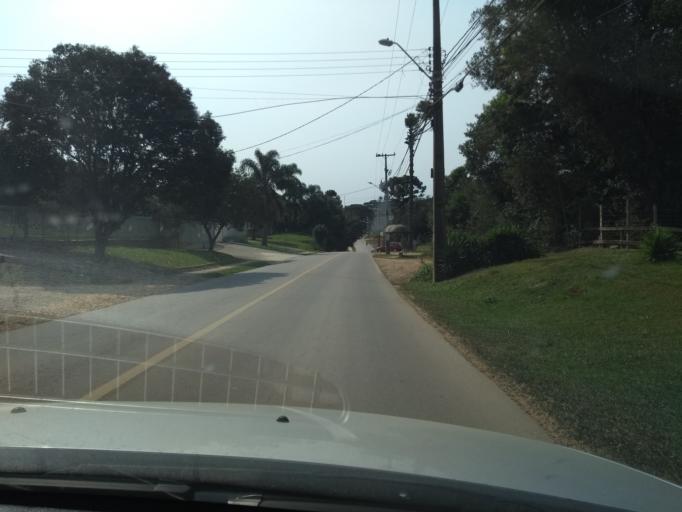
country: BR
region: Parana
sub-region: Araucaria
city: Araucaria
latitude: -25.6137
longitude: -49.3414
